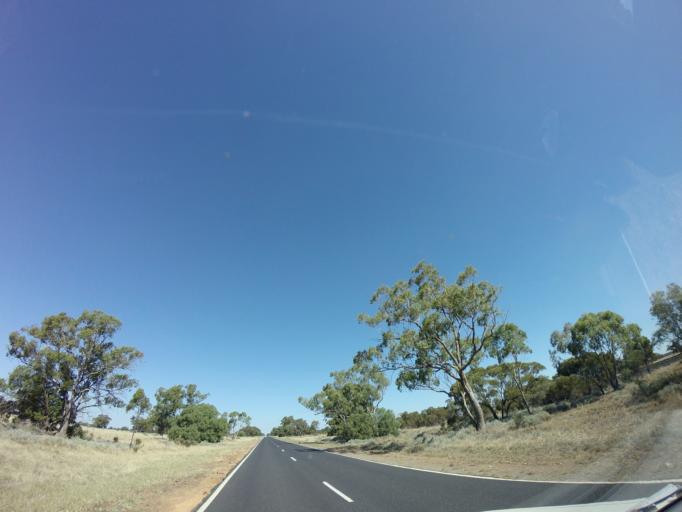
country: AU
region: New South Wales
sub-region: Bogan
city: Nyngan
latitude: -31.7824
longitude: 147.6125
